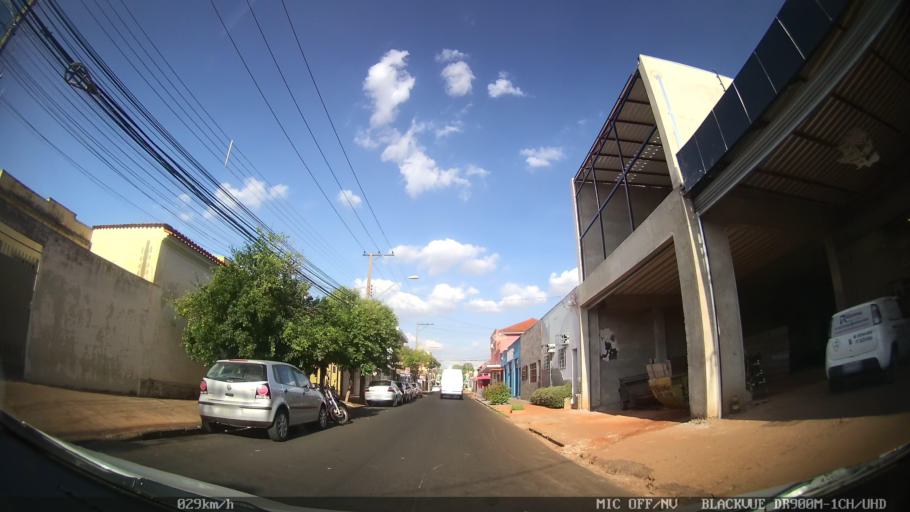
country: BR
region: Sao Paulo
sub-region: Ribeirao Preto
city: Ribeirao Preto
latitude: -21.1645
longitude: -47.8086
